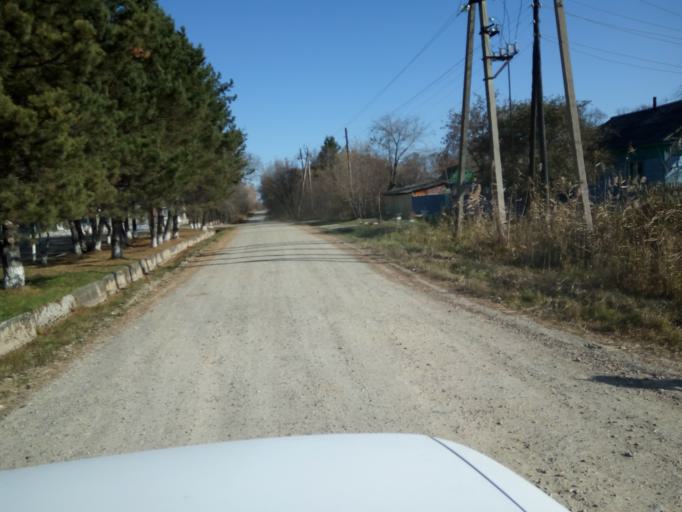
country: RU
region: Primorskiy
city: Lazo
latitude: 45.8751
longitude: 133.6496
